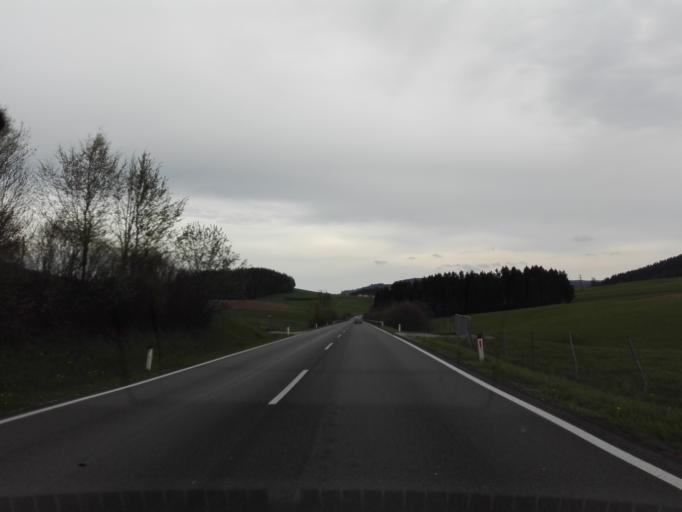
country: AT
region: Upper Austria
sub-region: Politischer Bezirk Rohrbach
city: Schlaegl
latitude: 48.5967
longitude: 13.9637
